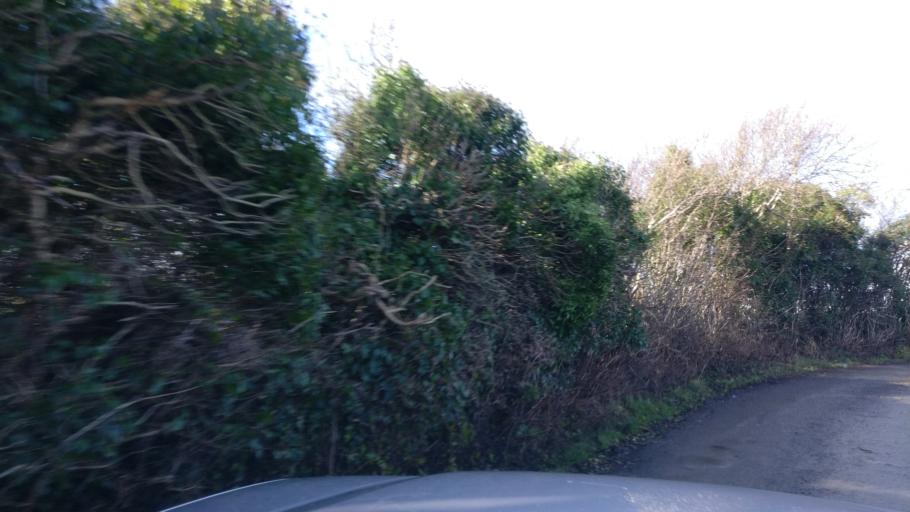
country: IE
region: Connaught
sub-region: County Galway
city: Athenry
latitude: 53.2305
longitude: -8.7591
